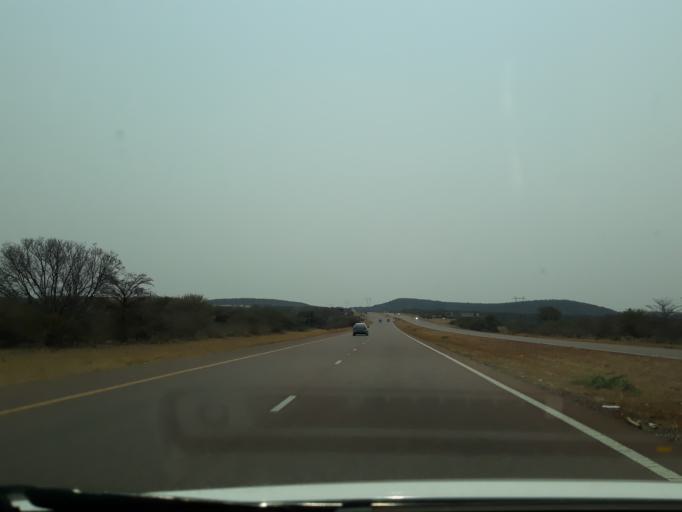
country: BW
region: Kgatleng
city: Bokaa
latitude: -24.4070
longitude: 26.0535
